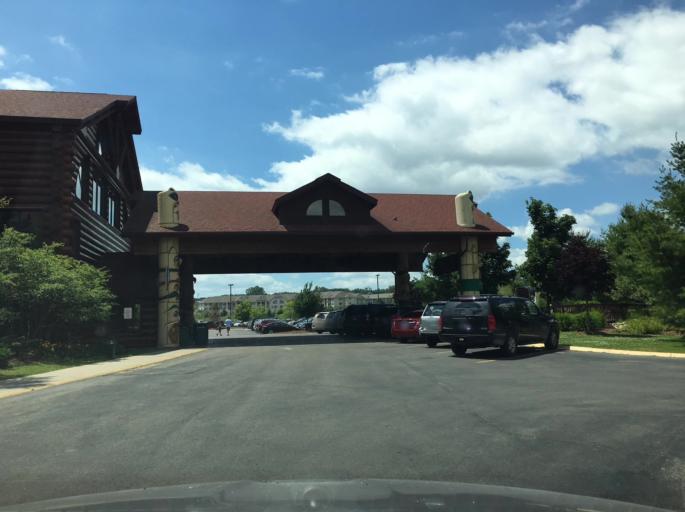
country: US
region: Michigan
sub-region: Grand Traverse County
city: Traverse City
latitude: 44.7394
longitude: -85.6475
